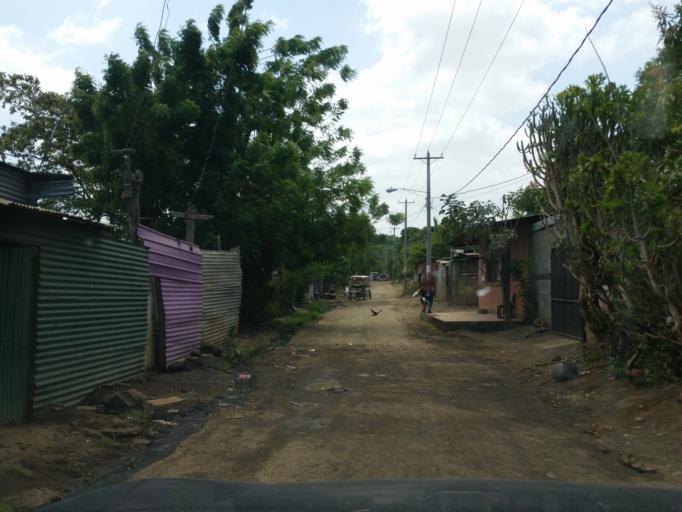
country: NI
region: Managua
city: Managua
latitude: 12.1414
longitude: -86.1913
